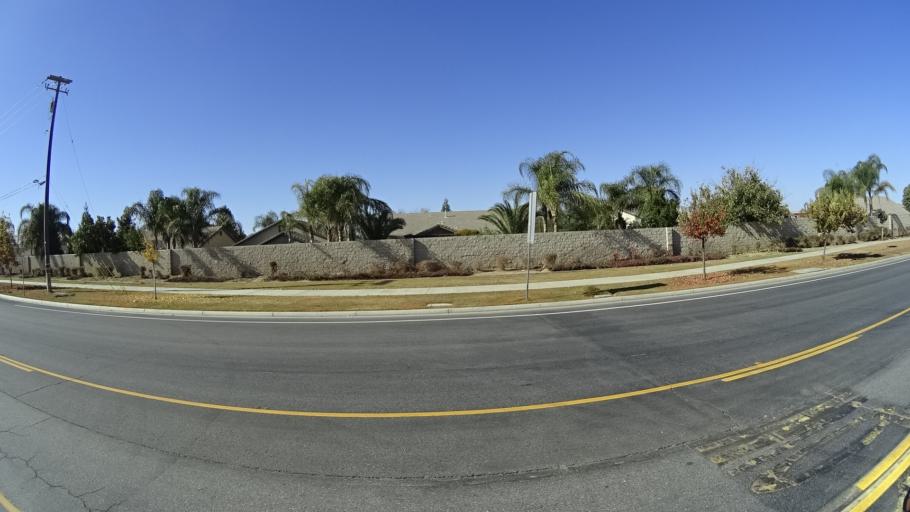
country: US
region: California
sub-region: Kern County
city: Greenfield
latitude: 35.2715
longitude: -119.0566
